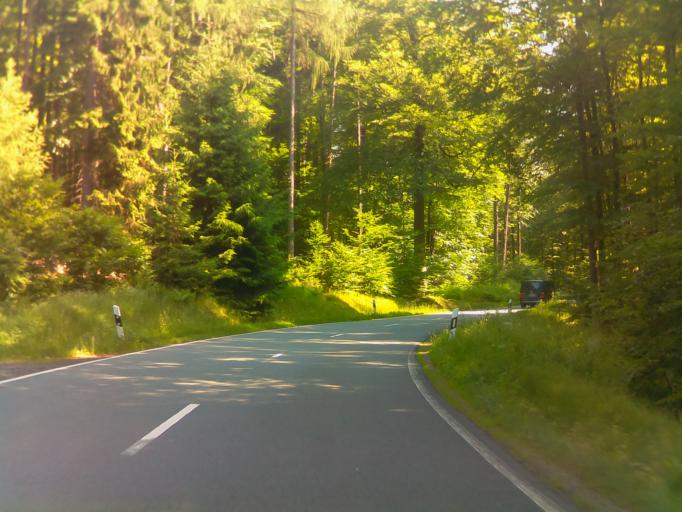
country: DE
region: Hesse
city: Rosenthal
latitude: 50.9464
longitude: 8.8496
